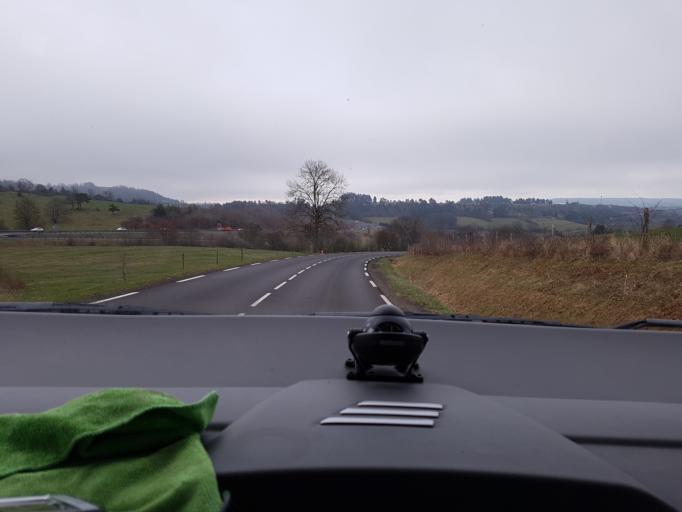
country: FR
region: Auvergne
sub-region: Departement du Cantal
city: Saint-Flour
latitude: 45.0564
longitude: 3.1086
